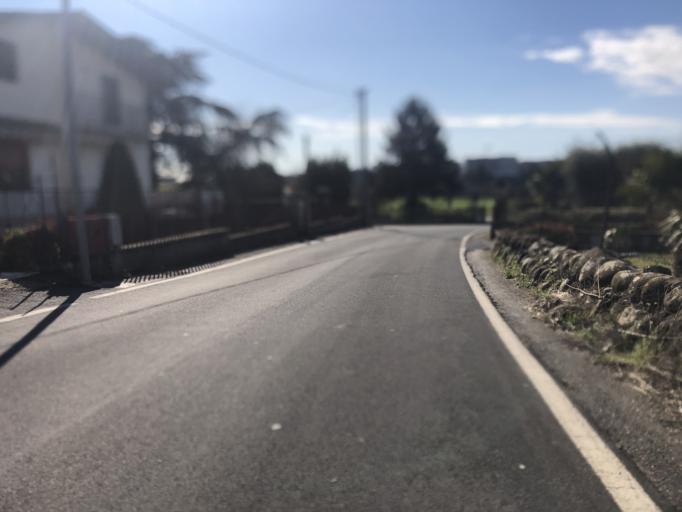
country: IT
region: Veneto
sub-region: Provincia di Verona
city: Bussolengo
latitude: 45.4851
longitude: 10.8473
